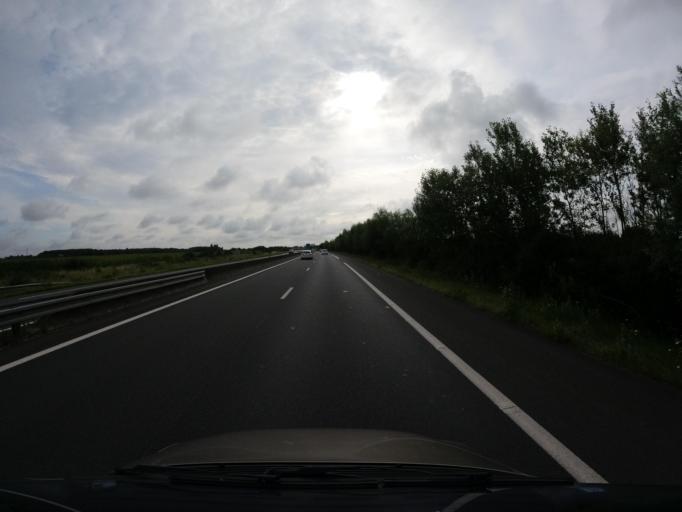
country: FR
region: Centre
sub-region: Departement d'Indre-et-Loire
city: Savonnieres
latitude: 47.3016
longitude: 0.5407
